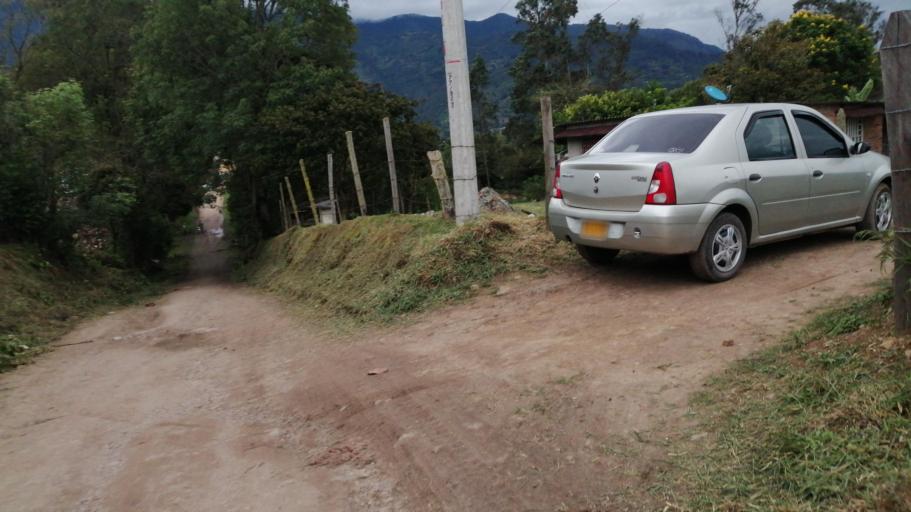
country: CO
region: Boyaca
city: Chinavita
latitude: 5.1385
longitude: -73.3947
